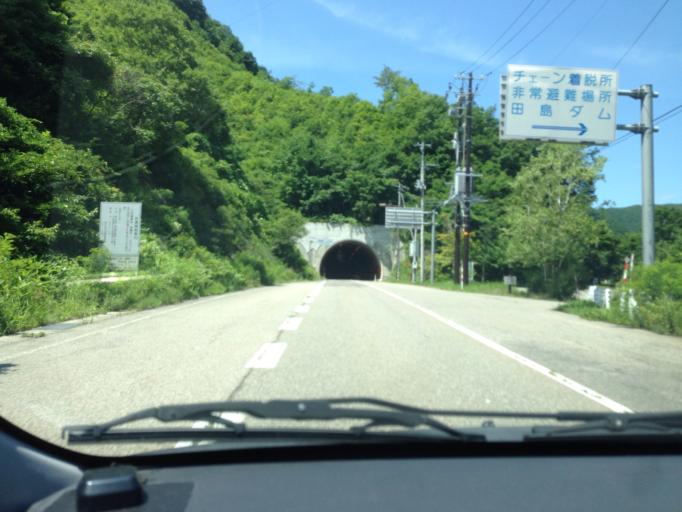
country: JP
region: Tochigi
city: Kuroiso
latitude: 37.2324
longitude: 139.7372
